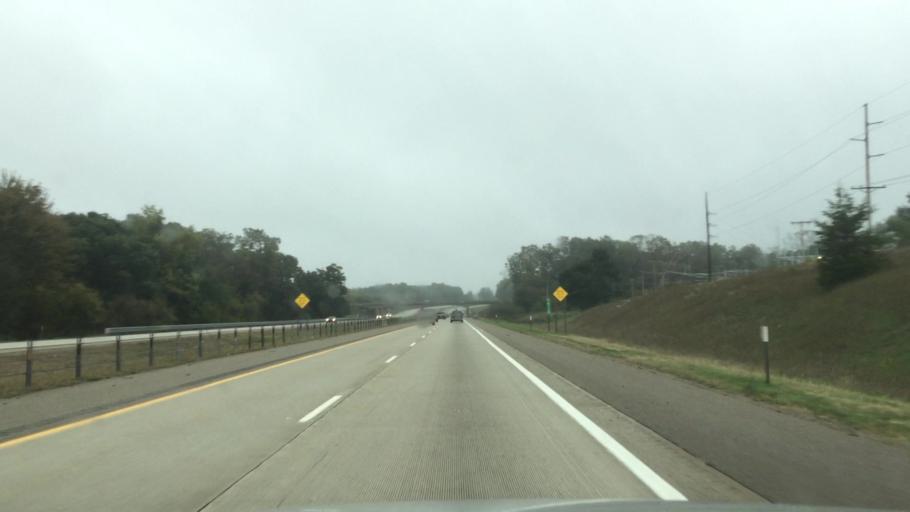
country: US
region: Michigan
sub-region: Van Buren County
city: Paw Paw
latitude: 42.2127
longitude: -85.8668
